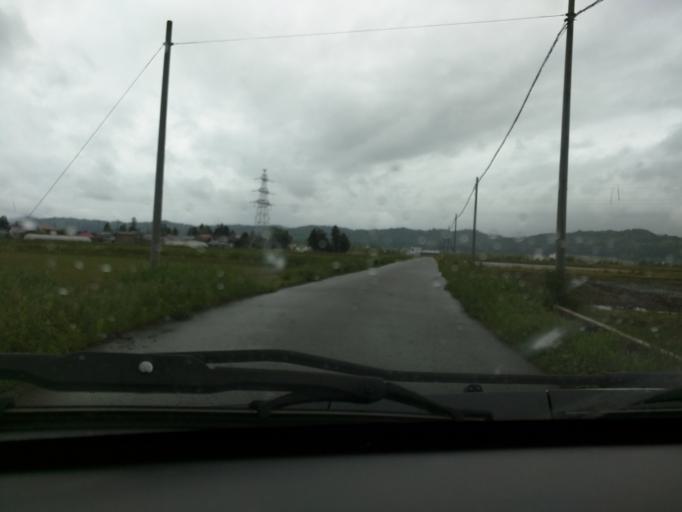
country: JP
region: Fukushima
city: Kitakata
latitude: 37.6343
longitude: 139.8644
